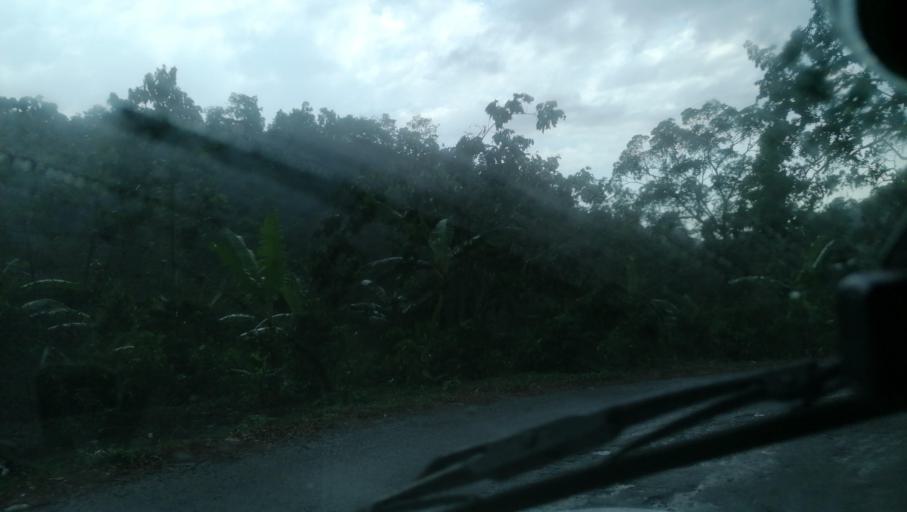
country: MX
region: Chiapas
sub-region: Cacahoatan
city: Benito Juarez
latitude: 15.0621
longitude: -92.1922
